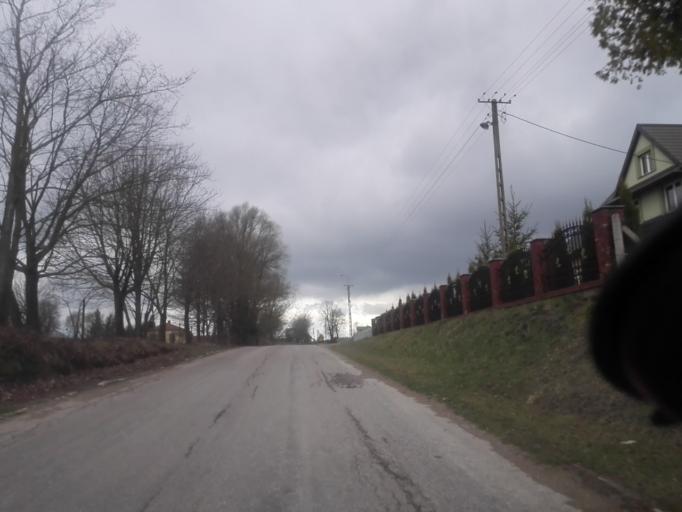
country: PL
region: Podlasie
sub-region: Suwalki
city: Suwalki
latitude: 54.2019
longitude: 22.9412
